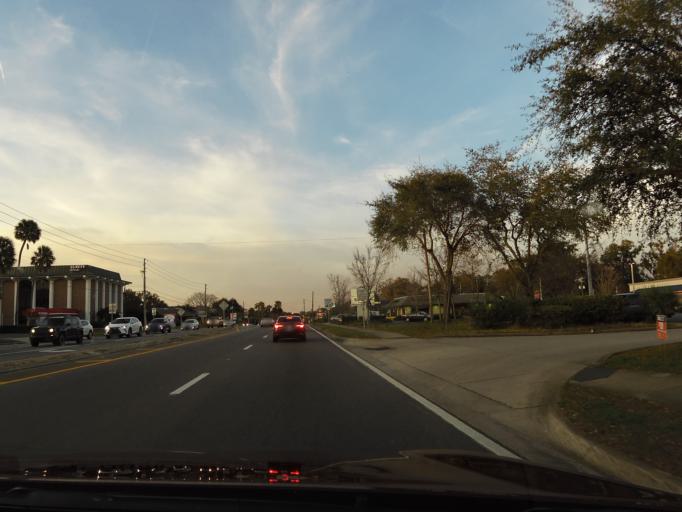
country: US
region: Florida
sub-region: Volusia County
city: North DeLand
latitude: 29.0433
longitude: -81.3038
